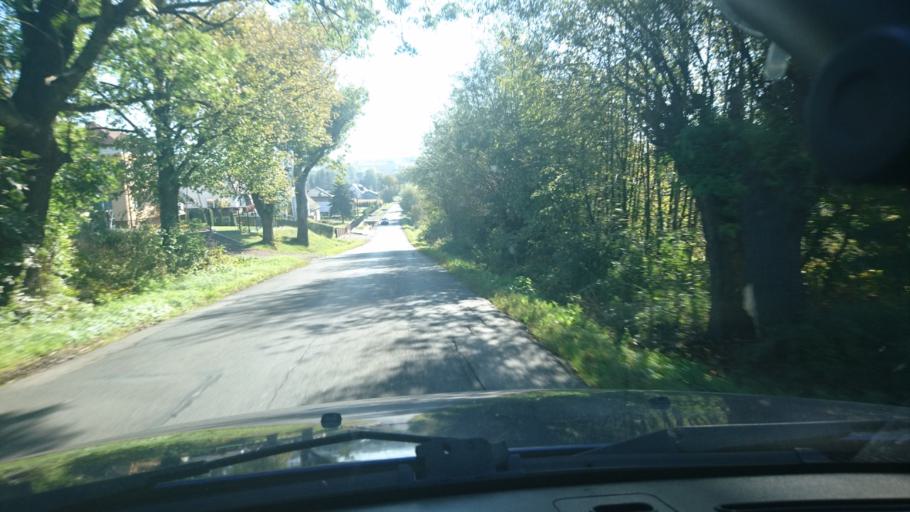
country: PL
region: Silesian Voivodeship
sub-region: Powiat bielski
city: Bronow
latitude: 49.8532
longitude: 18.9333
